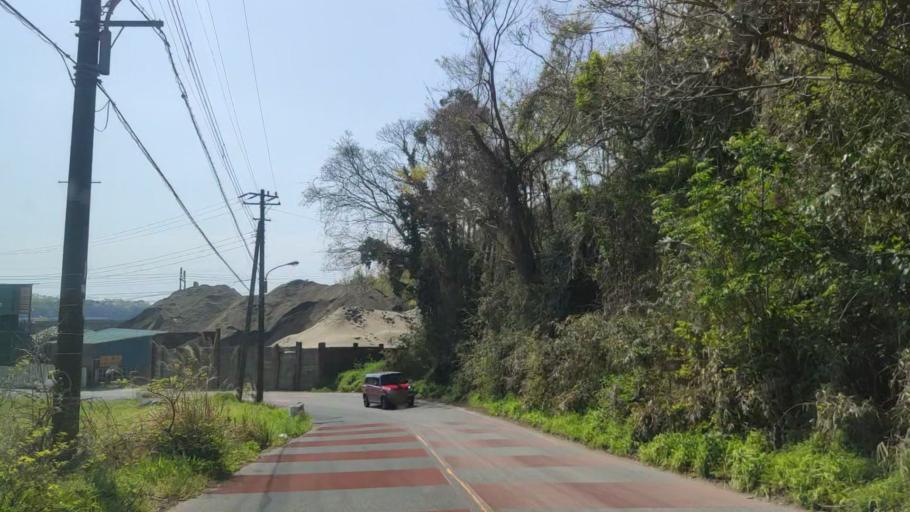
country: JP
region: Kanagawa
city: Ninomiya
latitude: 35.3178
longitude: 139.2748
